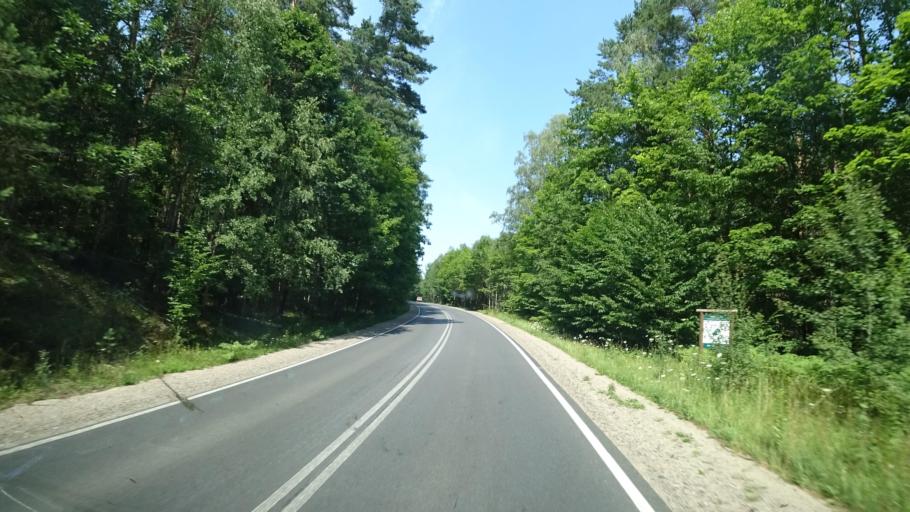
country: PL
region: Pomeranian Voivodeship
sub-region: Powiat koscierski
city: Dziemiany
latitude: 53.9835
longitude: 17.7739
